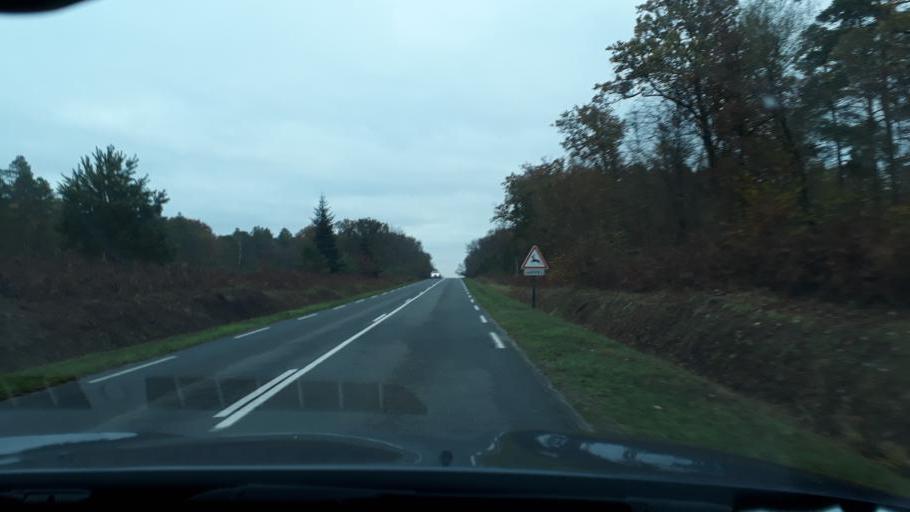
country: FR
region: Centre
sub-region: Departement du Loiret
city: Bouzy-la-Foret
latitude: 47.8320
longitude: 2.4236
